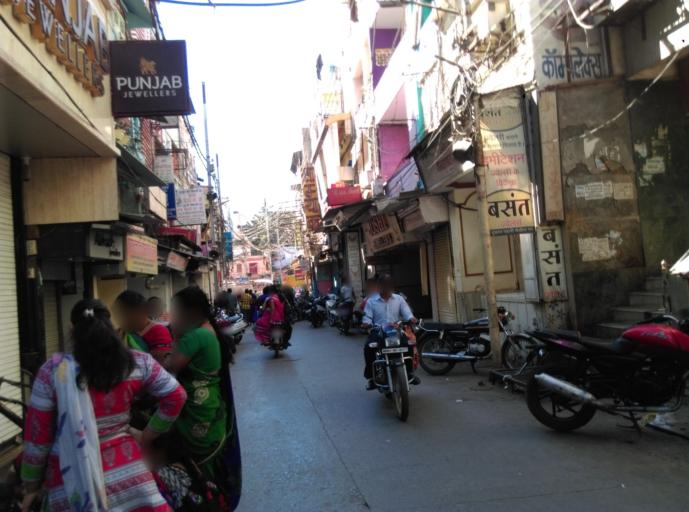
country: IN
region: Madhya Pradesh
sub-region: Indore
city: Indore
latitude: 22.7180
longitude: 75.8520
